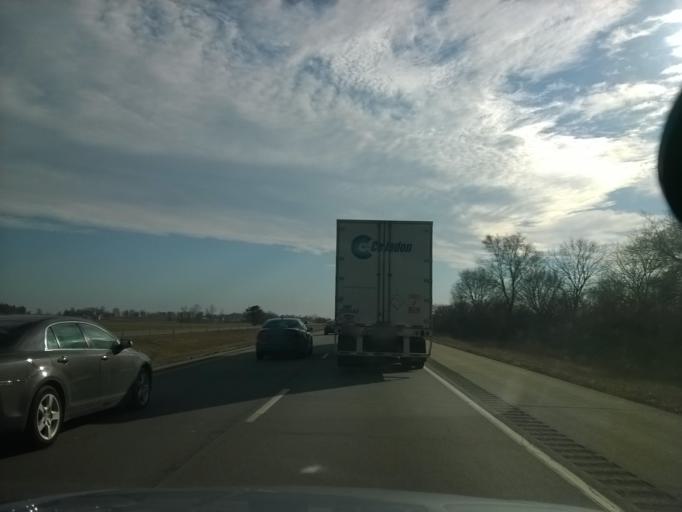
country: US
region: Indiana
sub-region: Johnson County
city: Edinburgh
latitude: 39.3753
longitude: -85.9428
